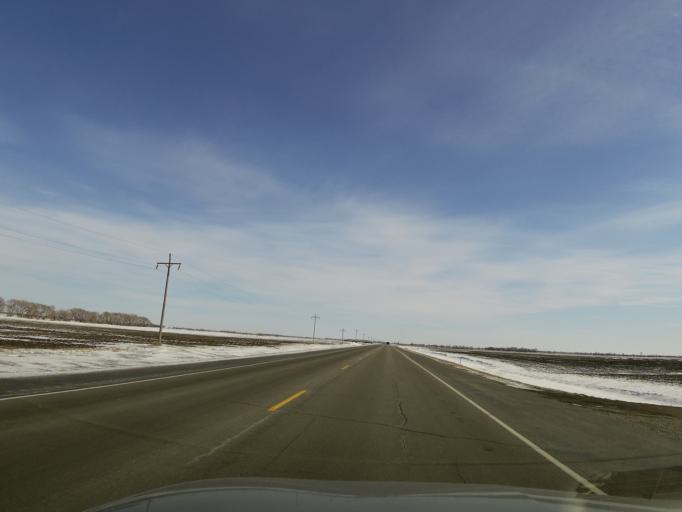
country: US
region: North Dakota
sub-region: Walsh County
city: Grafton
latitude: 48.4123
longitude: -97.3067
